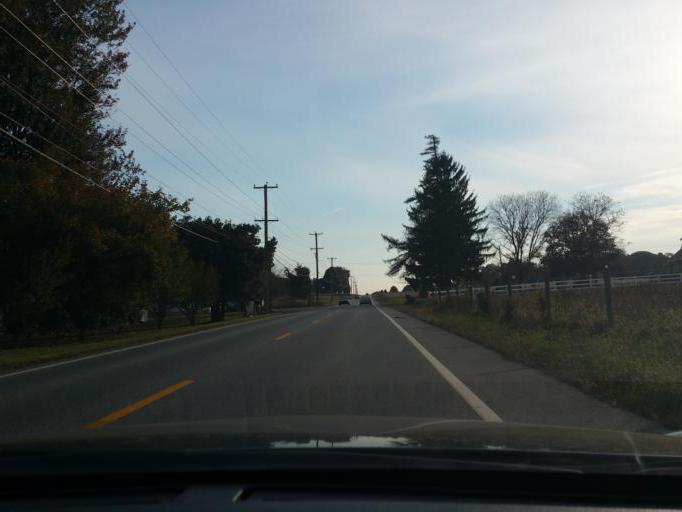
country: US
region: Maryland
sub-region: Cecil County
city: Rising Sun
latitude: 39.7011
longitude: -76.0426
